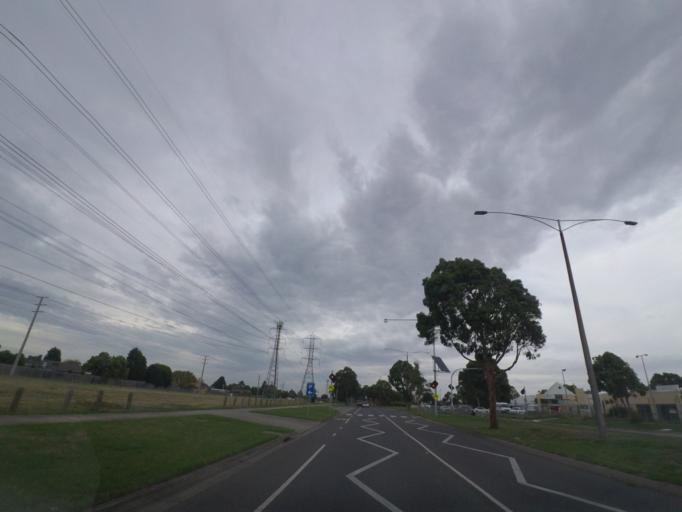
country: AU
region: Victoria
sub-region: Whittlesea
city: Mill Park
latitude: -37.6578
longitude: 145.0568
